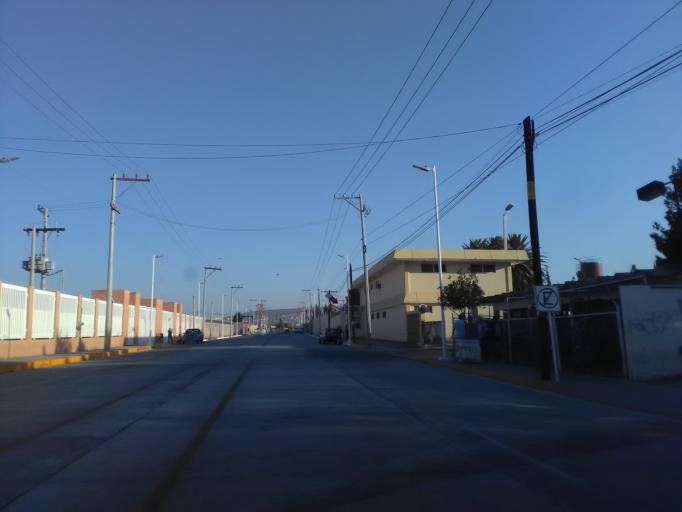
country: MX
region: Durango
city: Victoria de Durango
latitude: 24.0619
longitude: -104.6151
